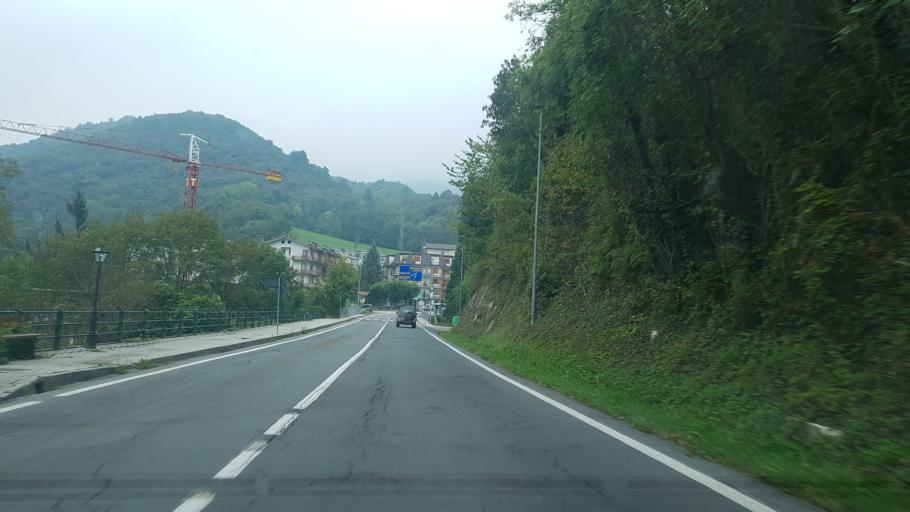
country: IT
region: Piedmont
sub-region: Provincia di Cuneo
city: Frabosa Sottana
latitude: 44.3045
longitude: 7.8004
